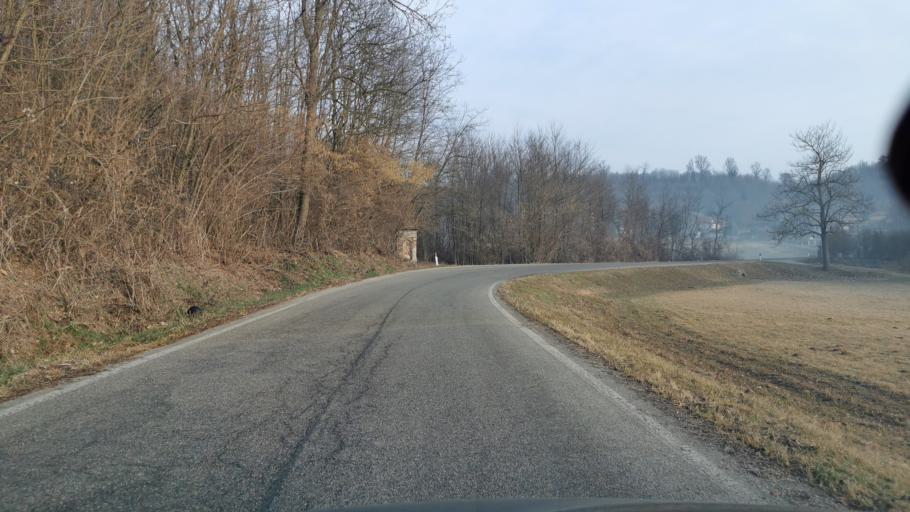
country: IT
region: Piedmont
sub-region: Provincia di Torino
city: Vialfre
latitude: 45.3743
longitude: 7.8221
